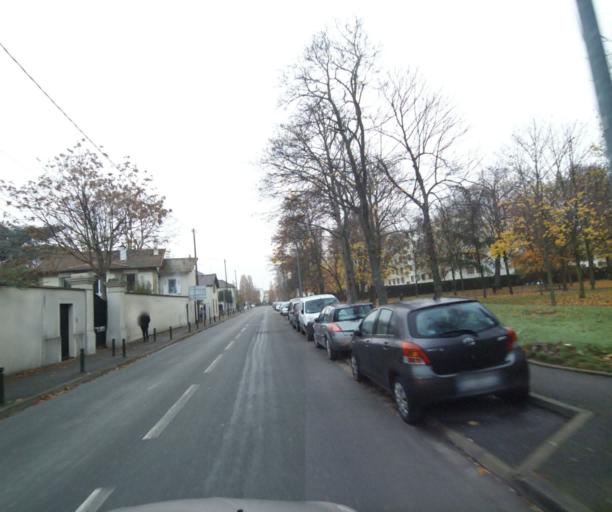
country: FR
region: Ile-de-France
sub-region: Departement du Val-de-Marne
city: Bry-sur-Marne
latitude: 48.8561
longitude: 2.5265
